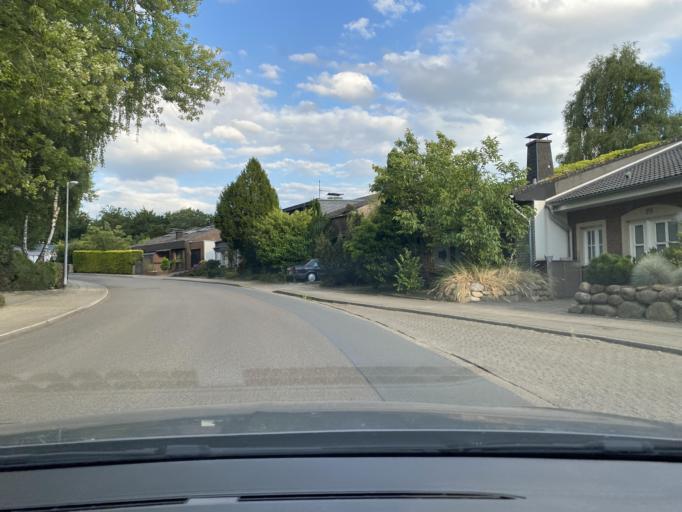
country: DE
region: North Rhine-Westphalia
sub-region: Regierungsbezirk Dusseldorf
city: Heiligenhaus
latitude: 51.3737
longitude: 6.9441
